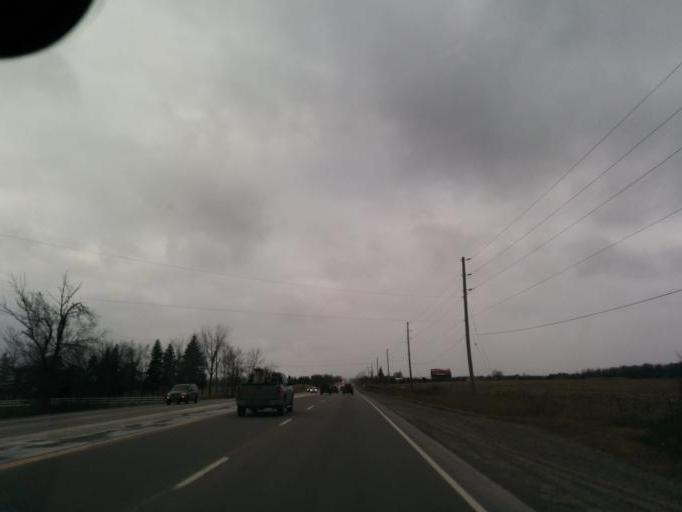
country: CA
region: Ontario
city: Brampton
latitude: 43.7577
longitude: -79.8568
